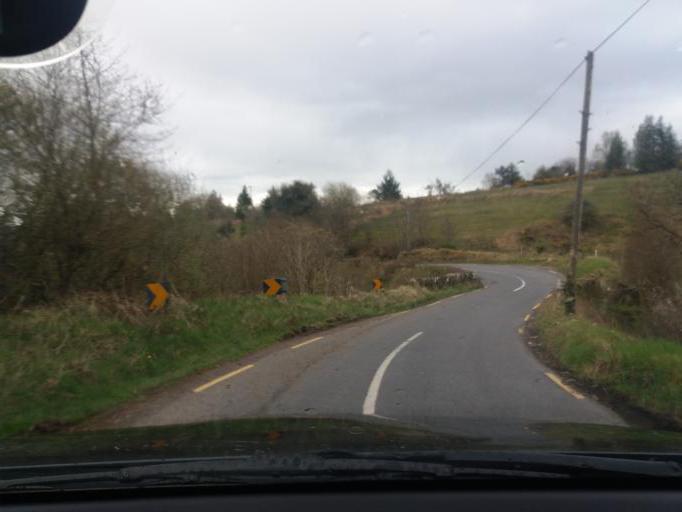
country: IE
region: Ulster
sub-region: An Cabhan
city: Ballyconnell
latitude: 54.1575
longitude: -7.7643
